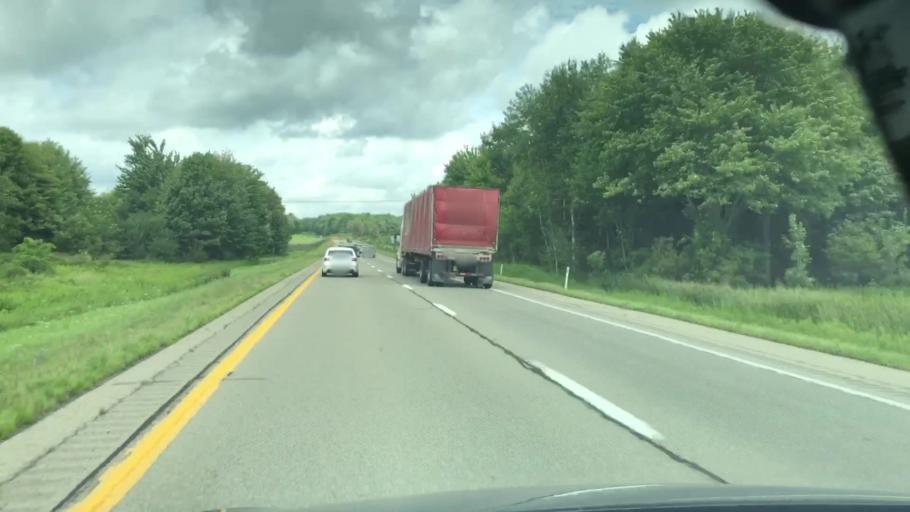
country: US
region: Pennsylvania
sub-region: Erie County
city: Edinboro
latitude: 41.7784
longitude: -80.1838
